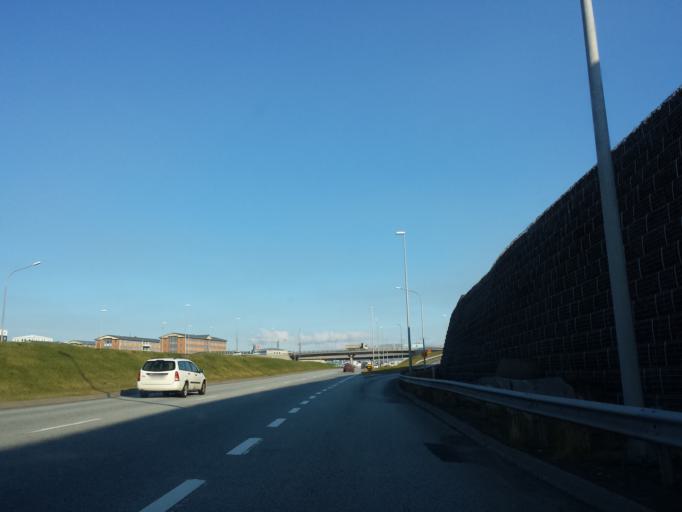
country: IS
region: Capital Region
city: Kopavogur
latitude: 64.0927
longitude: -21.8902
